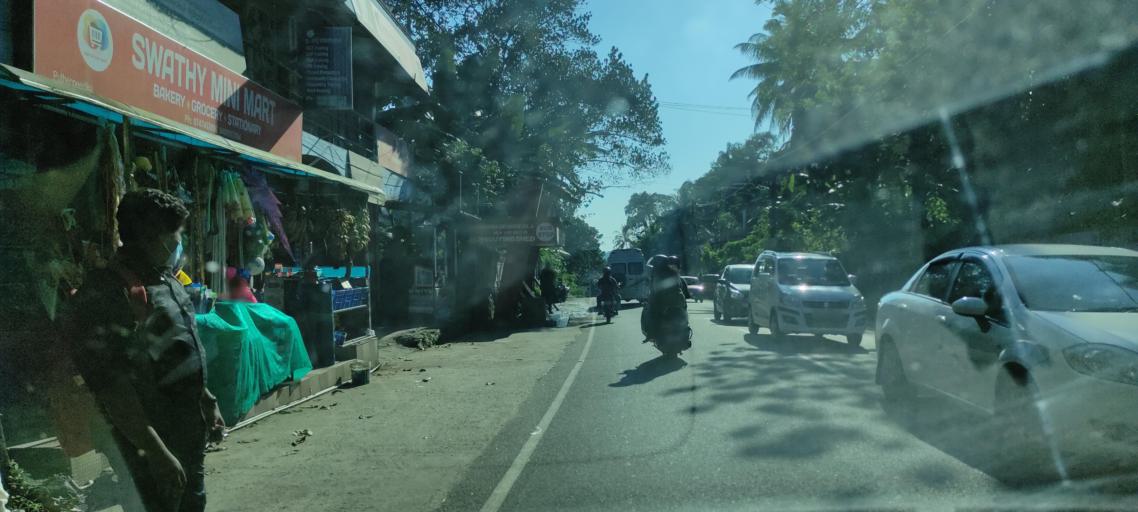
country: IN
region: Kerala
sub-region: Pattanamtitta
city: Pathanamthitta
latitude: 9.2550
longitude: 76.7626
